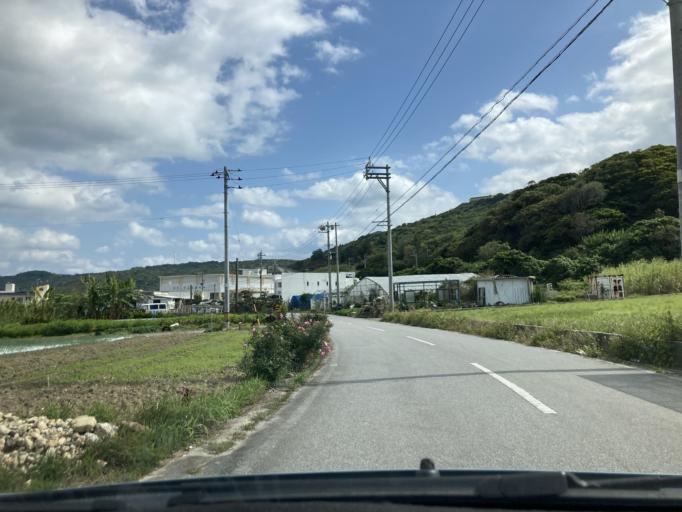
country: JP
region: Okinawa
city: Ginowan
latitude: 26.1680
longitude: 127.7815
